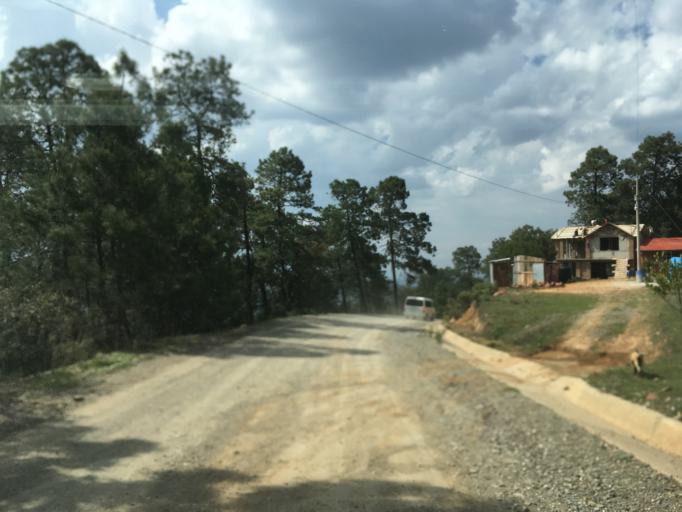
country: MX
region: Oaxaca
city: Santiago Tilantongo
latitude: 17.2067
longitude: -97.2787
